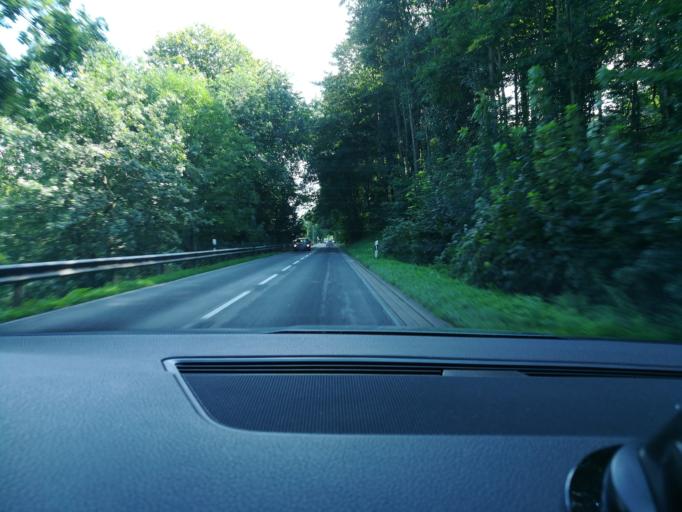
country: DE
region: North Rhine-Westphalia
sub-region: Regierungsbezirk Detmold
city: Hille
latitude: 52.2752
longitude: 8.7643
